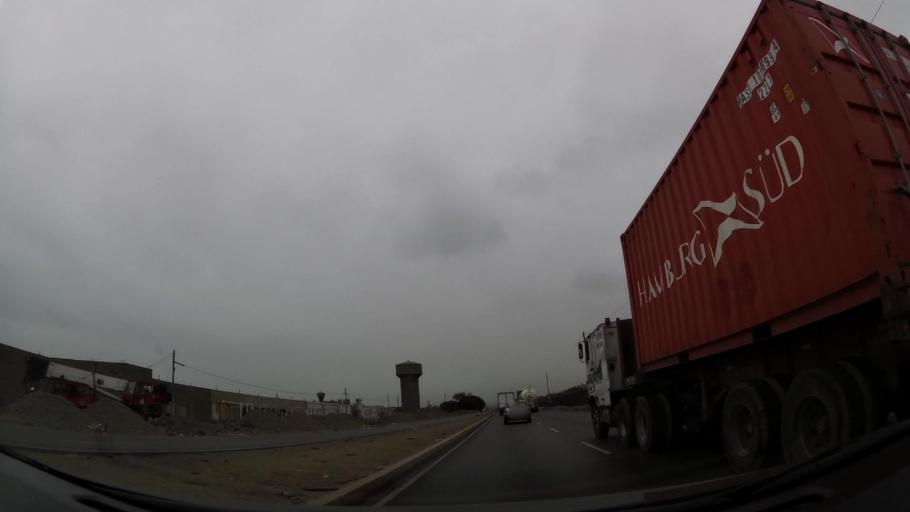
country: PE
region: Callao
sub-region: Callao
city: Callao
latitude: -12.0076
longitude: -77.1277
